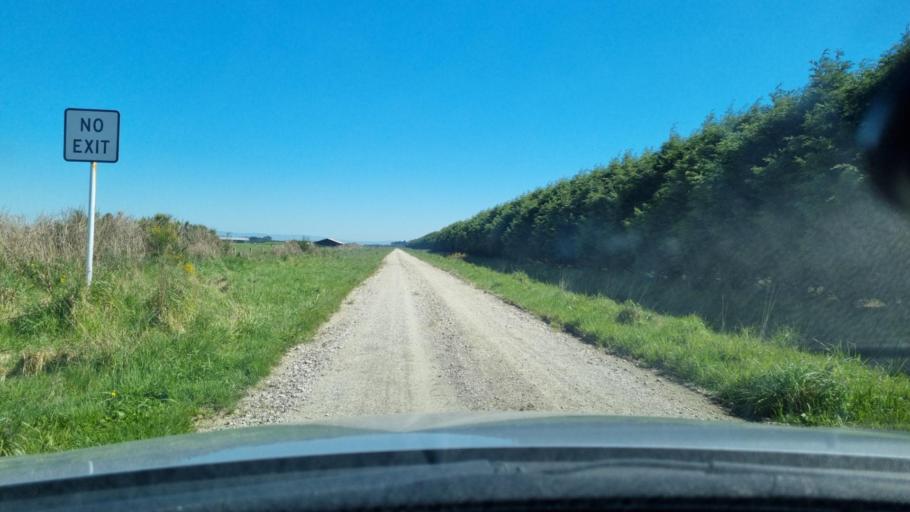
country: NZ
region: Southland
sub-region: Invercargill City
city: Invercargill
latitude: -46.4262
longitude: 168.3182
